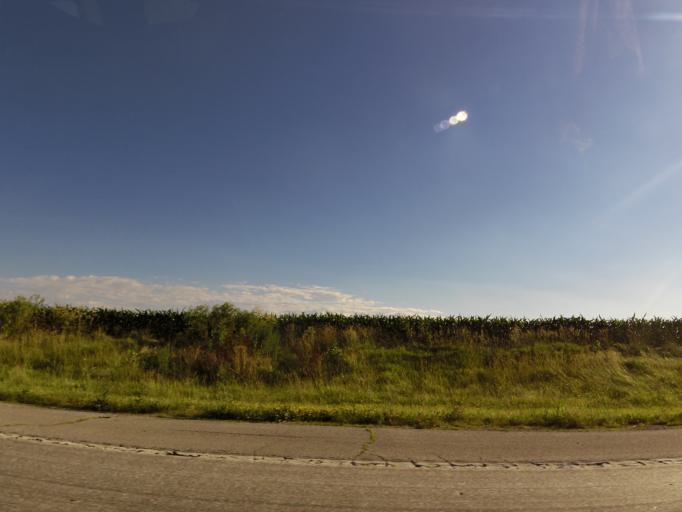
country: US
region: Missouri
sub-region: Pike County
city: Bowling Green
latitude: 39.3237
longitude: -91.1660
